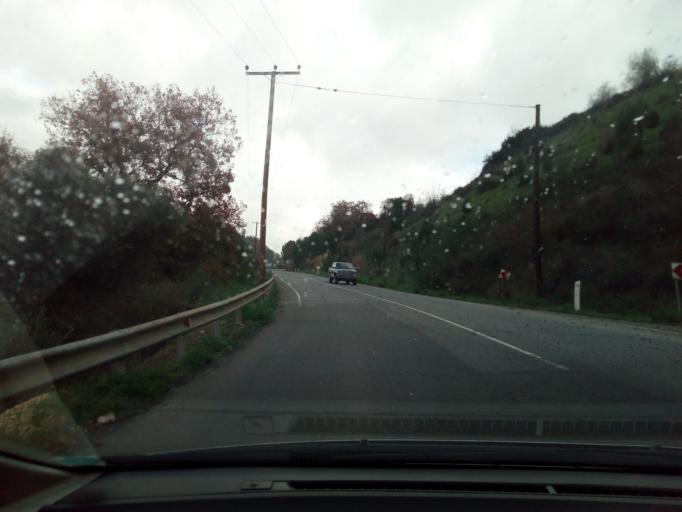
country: CY
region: Pafos
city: Tala
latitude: 34.9322
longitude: 32.4728
